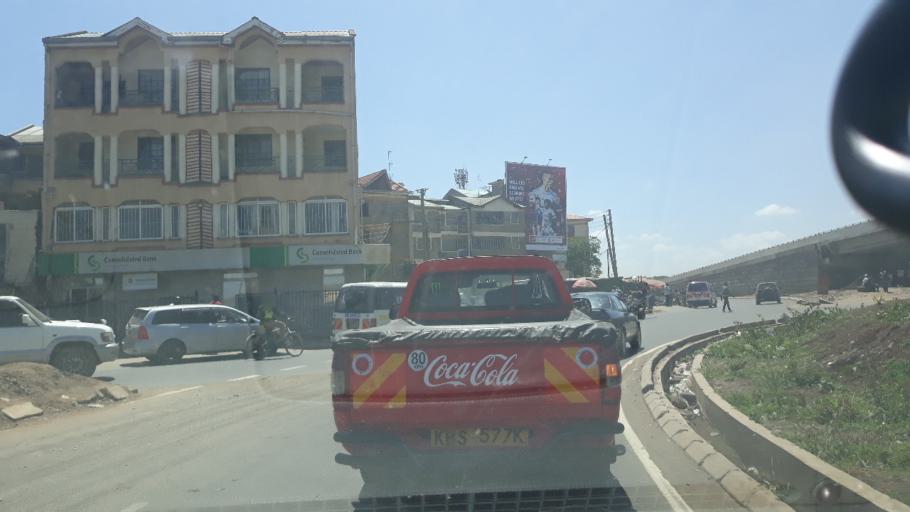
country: KE
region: Nairobi Area
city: Pumwani
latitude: -1.2784
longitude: 36.8830
